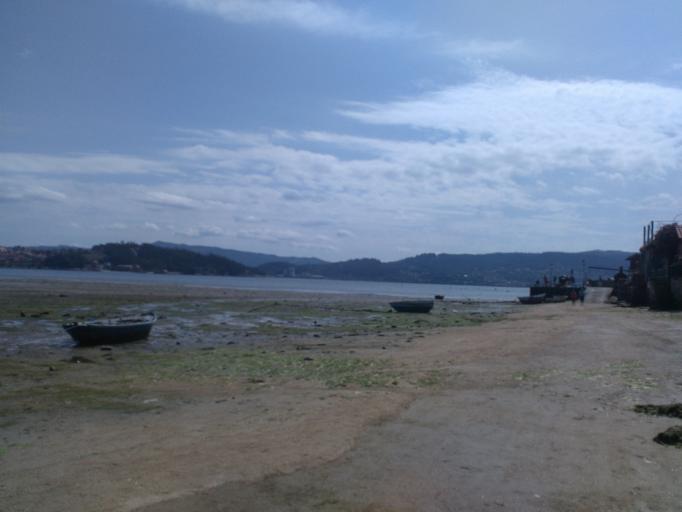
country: ES
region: Galicia
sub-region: Provincia de Pontevedra
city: Combarro
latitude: 42.4332
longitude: -8.7050
